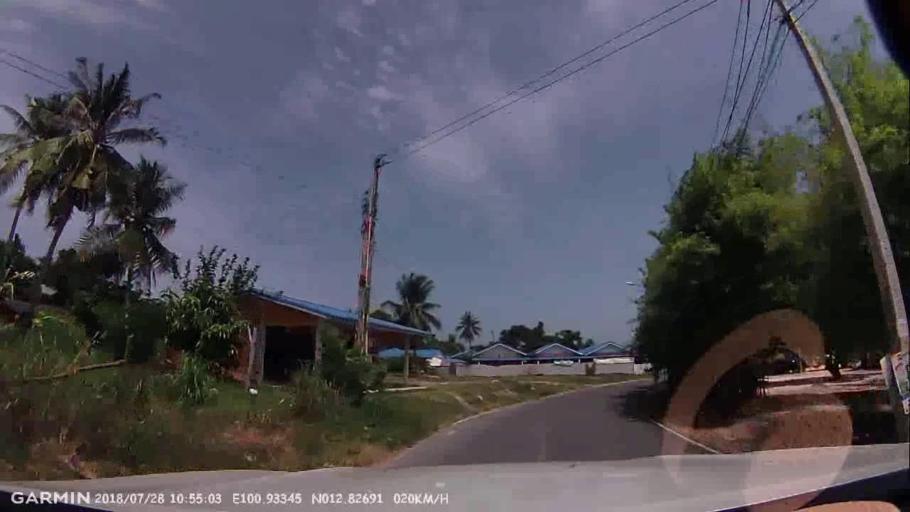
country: TH
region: Chon Buri
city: Phatthaya
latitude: 12.8270
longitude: 100.9334
